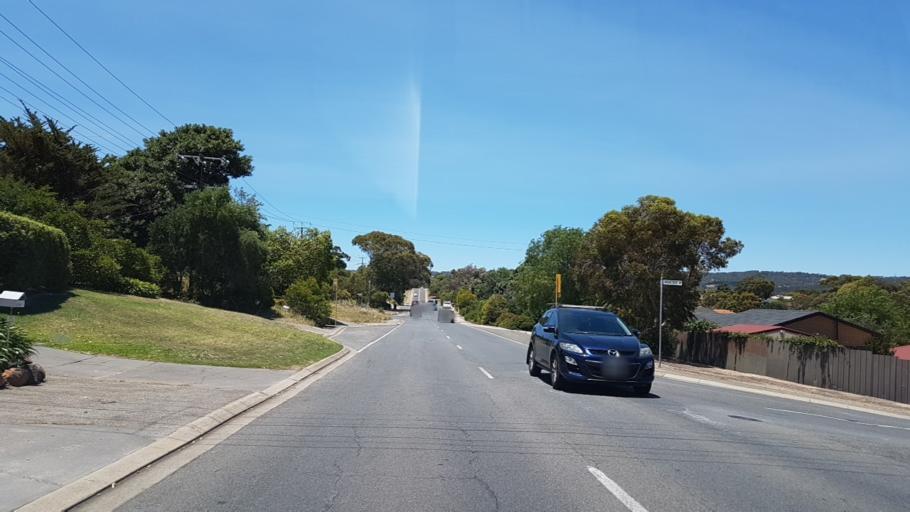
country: AU
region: South Australia
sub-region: Marion
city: Trott Park
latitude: -35.0830
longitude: 138.5510
